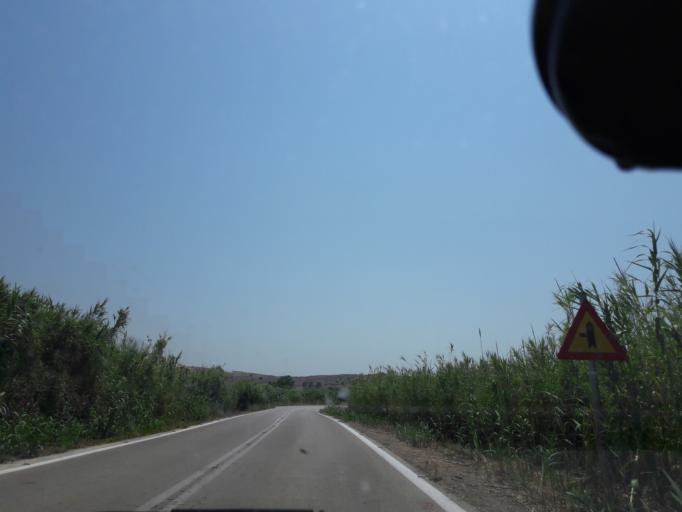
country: GR
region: North Aegean
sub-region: Nomos Lesvou
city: Myrina
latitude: 39.9227
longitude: 25.3116
